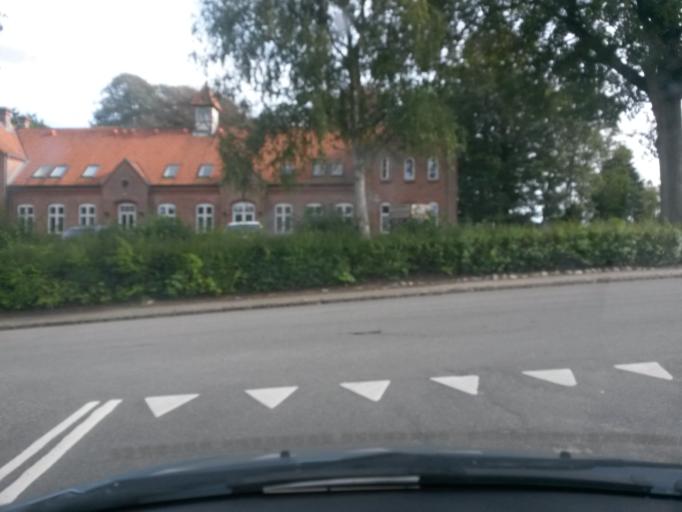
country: DK
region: Central Jutland
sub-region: Silkeborg Kommune
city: Kjellerup
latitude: 56.2912
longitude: 9.4339
